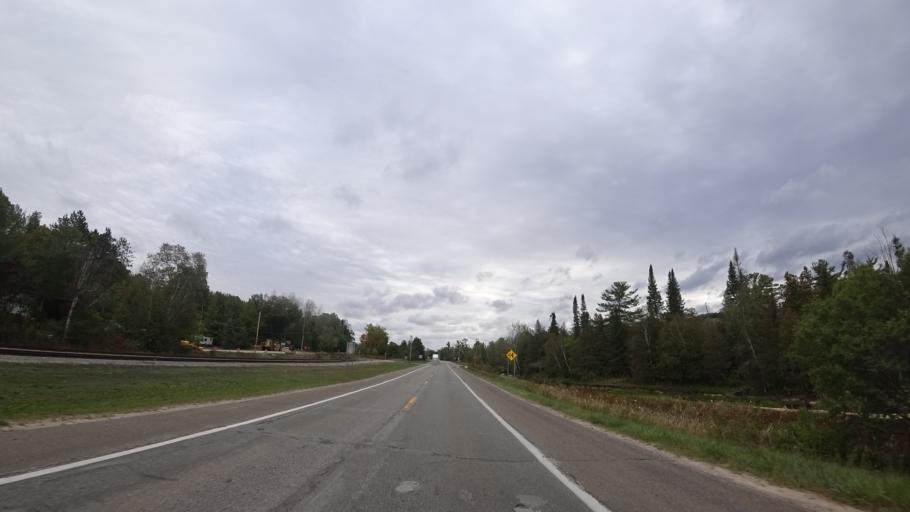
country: US
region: Michigan
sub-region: Charlevoix County
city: Boyne City
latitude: 45.1625
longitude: -84.9184
